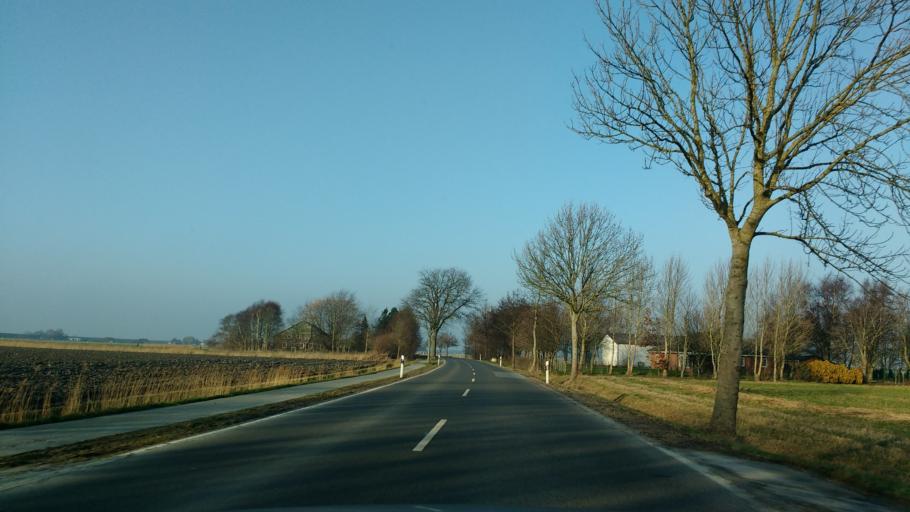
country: DE
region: Schleswig-Holstein
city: Friedrichskoog
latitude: 53.9872
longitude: 8.9112
